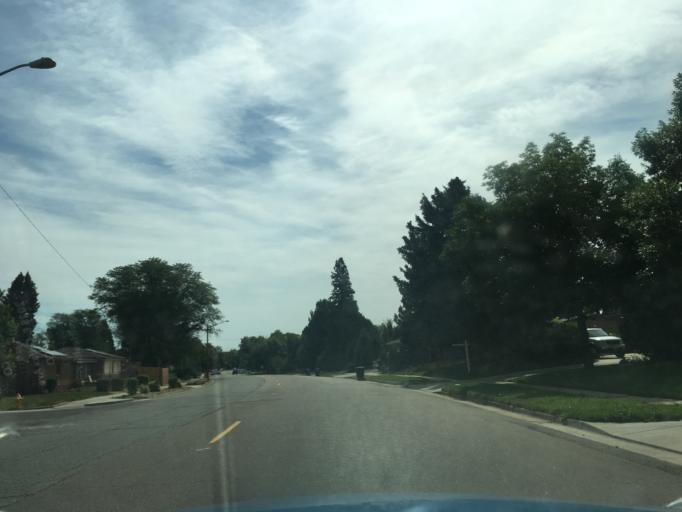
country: US
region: Colorado
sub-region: Arapahoe County
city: Sheridan
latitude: 39.6791
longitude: -105.0473
